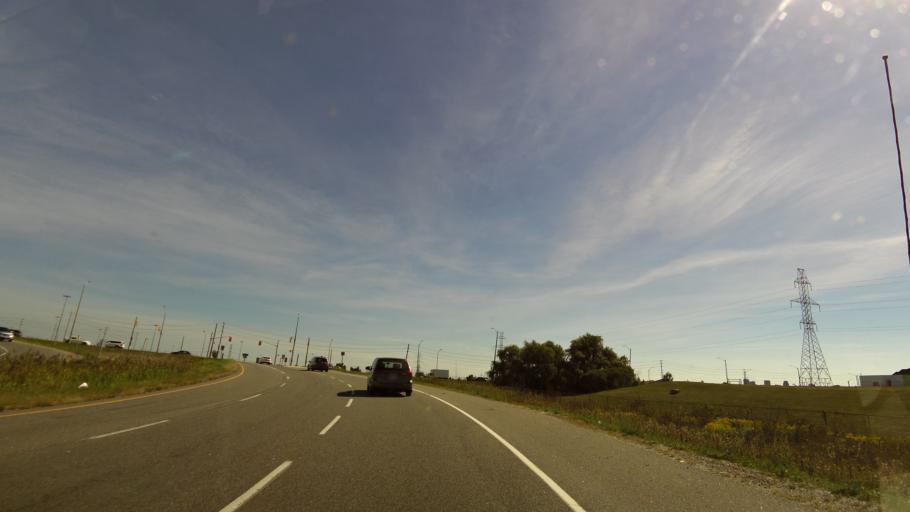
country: CA
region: Ontario
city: Mississauga
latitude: 43.6212
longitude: -79.6389
